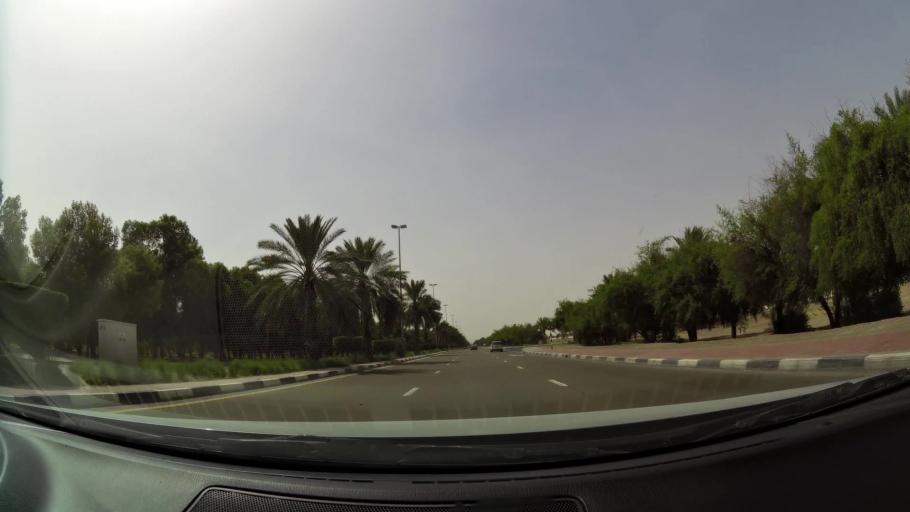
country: AE
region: Abu Dhabi
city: Al Ain
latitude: 24.1772
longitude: 55.6634
